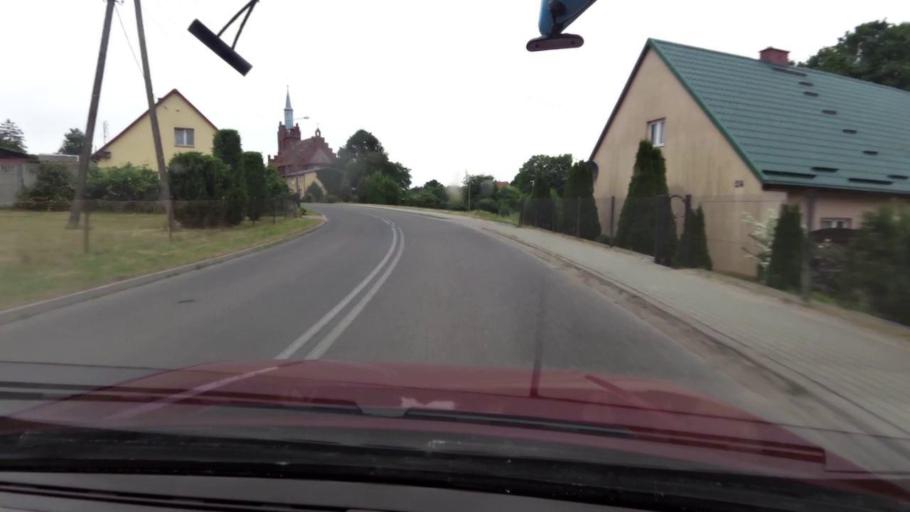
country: PL
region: West Pomeranian Voivodeship
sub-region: Powiat koszalinski
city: Sianow
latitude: 54.1793
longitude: 16.3840
